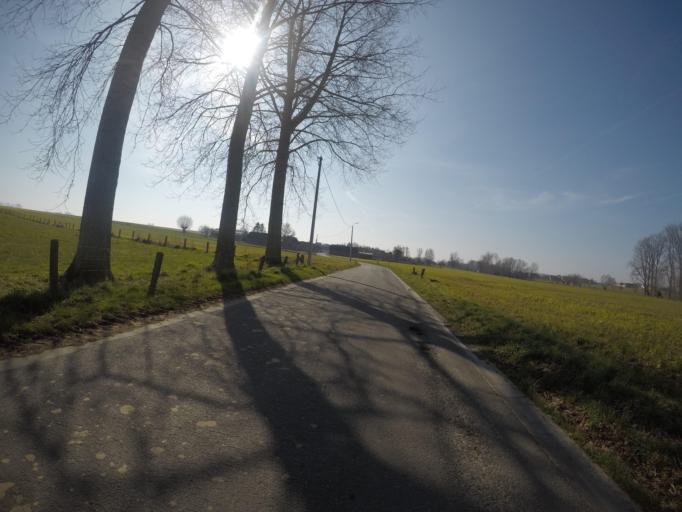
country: BE
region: Flanders
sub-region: Provincie Oost-Vlaanderen
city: Sint-Maria-Lierde
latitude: 50.7952
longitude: 3.8406
